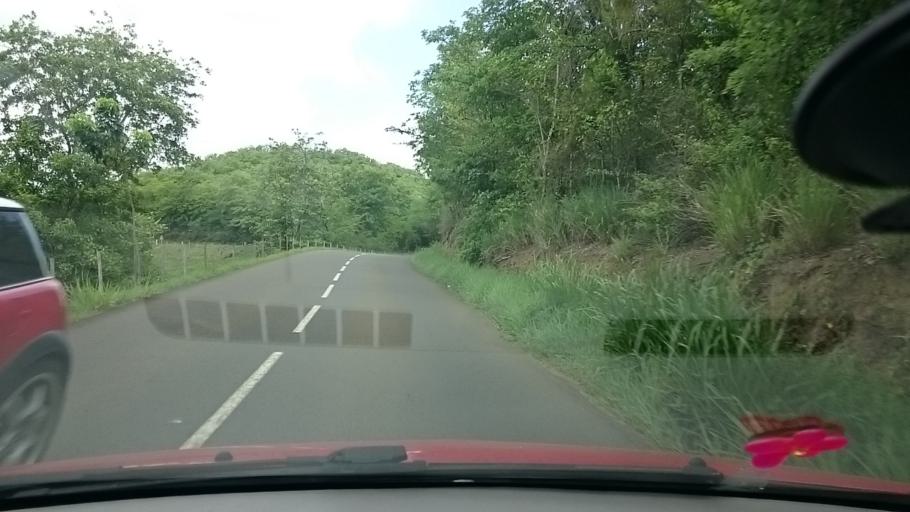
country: MQ
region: Martinique
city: Petite Riviere Salee
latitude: 14.7572
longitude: -60.9319
